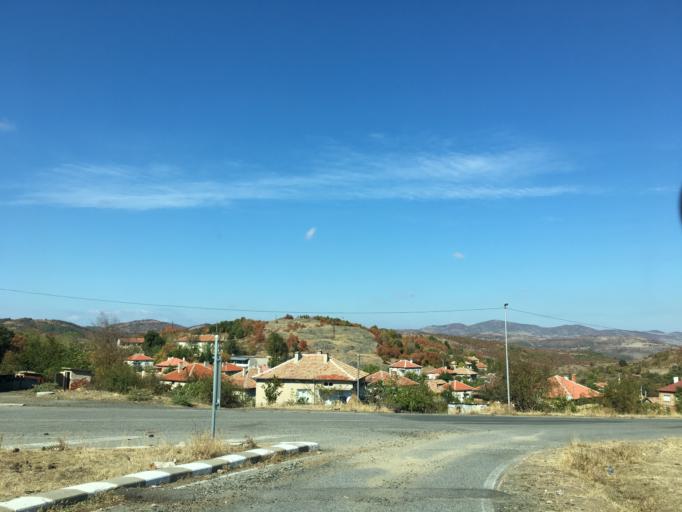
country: BG
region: Kurdzhali
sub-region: Obshtina Krumovgrad
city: Krumovgrad
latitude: 41.4710
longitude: 25.5235
